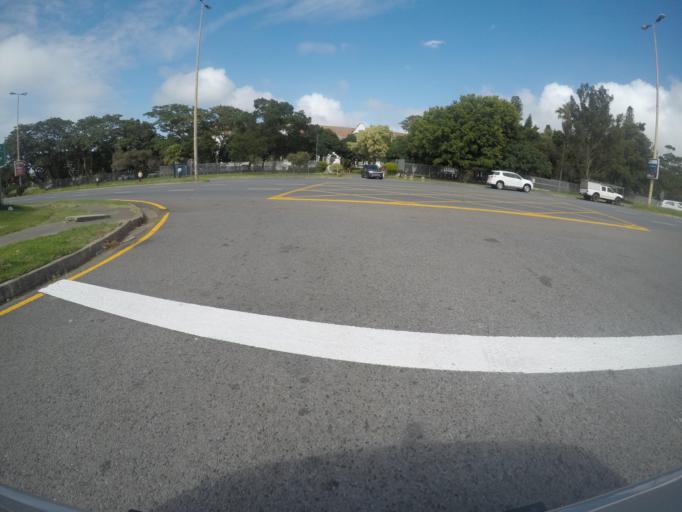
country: ZA
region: Eastern Cape
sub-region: Buffalo City Metropolitan Municipality
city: East London
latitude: -32.9943
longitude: 27.8967
